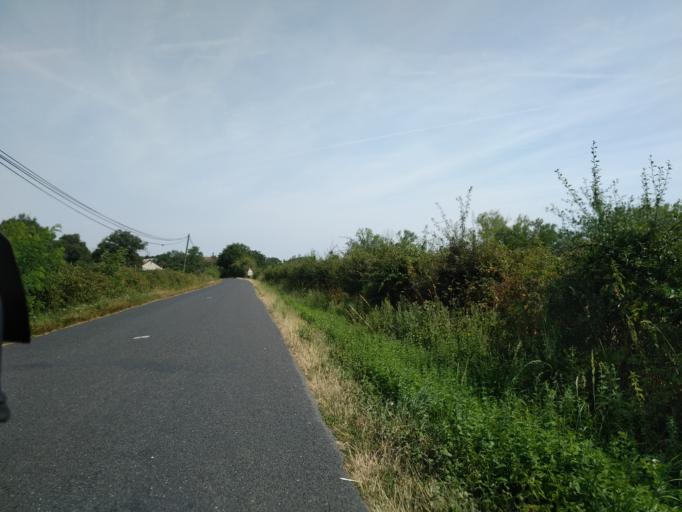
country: FR
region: Auvergne
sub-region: Departement de l'Allier
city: Molinet
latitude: 46.4191
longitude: 3.9766
